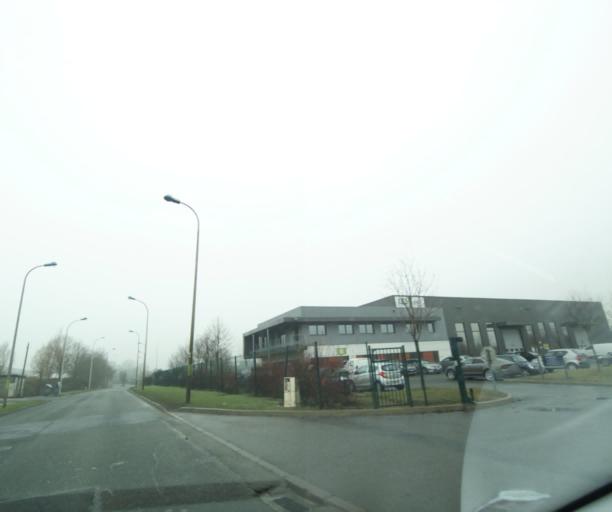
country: FR
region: Ile-de-France
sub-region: Departement de Seine-et-Marne
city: Dammartin-en-Goele
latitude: 49.0622
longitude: 2.7022
